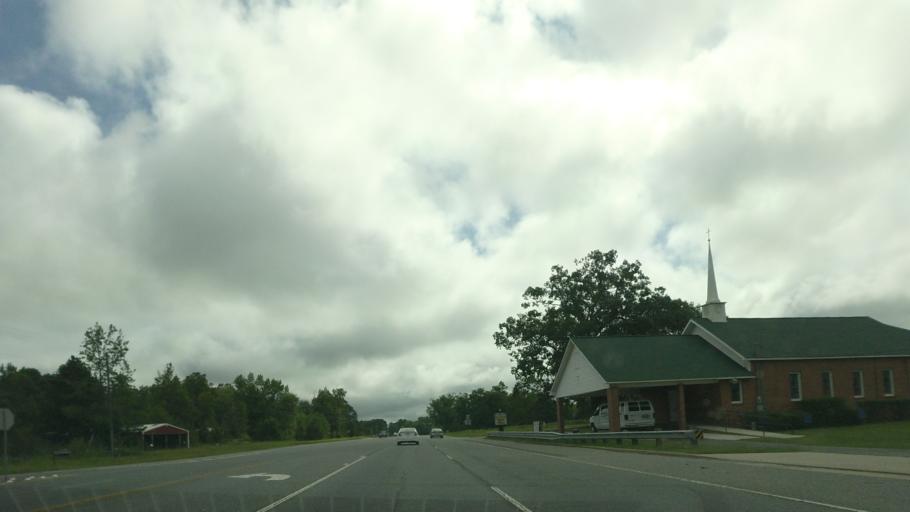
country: US
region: Georgia
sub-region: Laurens County
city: Dublin
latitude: 32.5506
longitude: -82.9930
